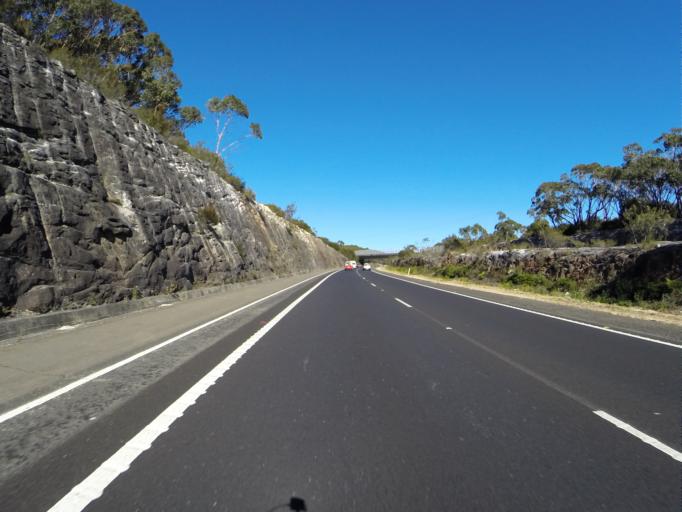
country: AU
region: New South Wales
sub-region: Wollongong
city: Helensburgh
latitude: -34.2405
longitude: 150.9451
